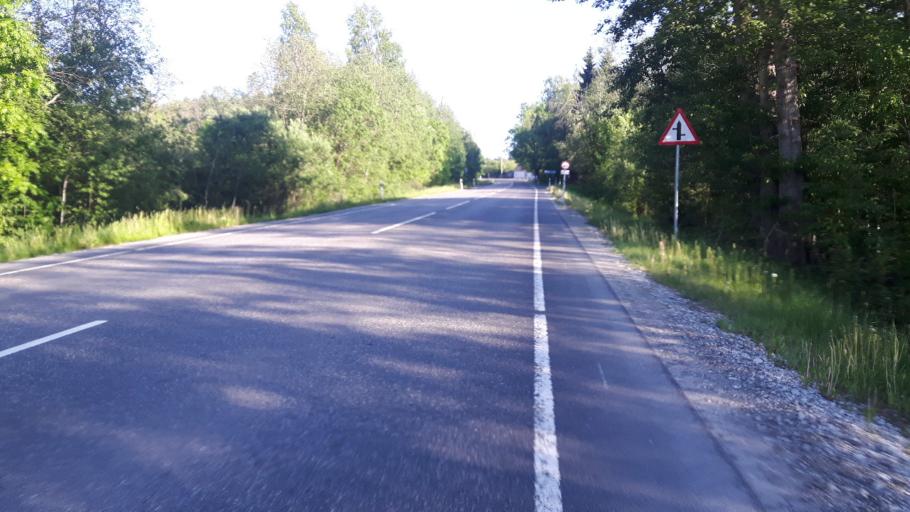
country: EE
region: Raplamaa
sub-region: Kehtna vald
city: Kehtna
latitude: 58.9060
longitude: 24.8862
